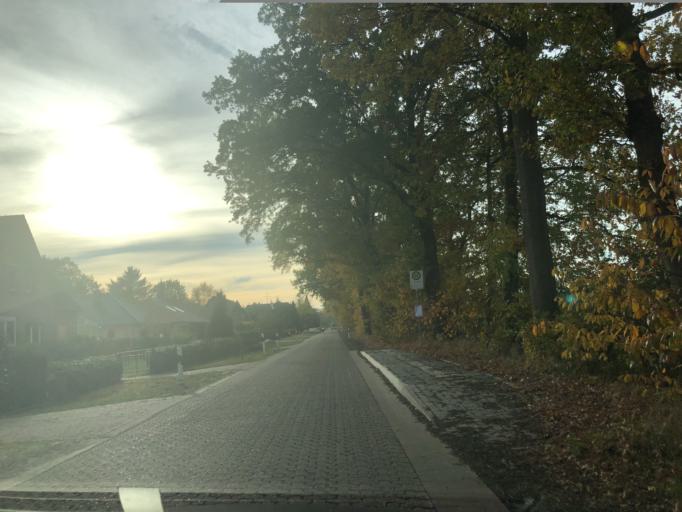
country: DE
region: Lower Saxony
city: Edewecht
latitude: 53.0938
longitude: 8.0827
